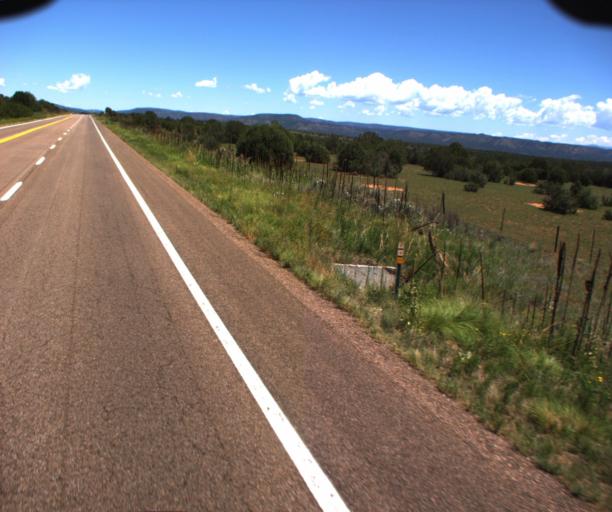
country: US
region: Arizona
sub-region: Navajo County
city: Cibecue
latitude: 33.9604
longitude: -110.3275
